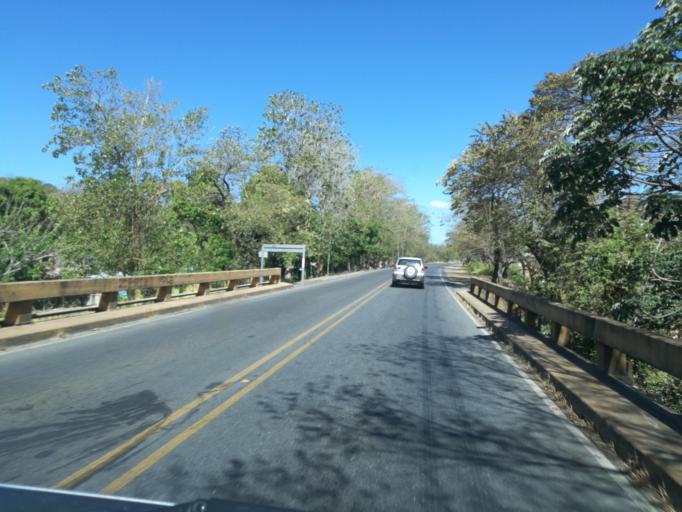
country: CR
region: Guanacaste
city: Liberia
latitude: 10.6501
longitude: -85.4632
